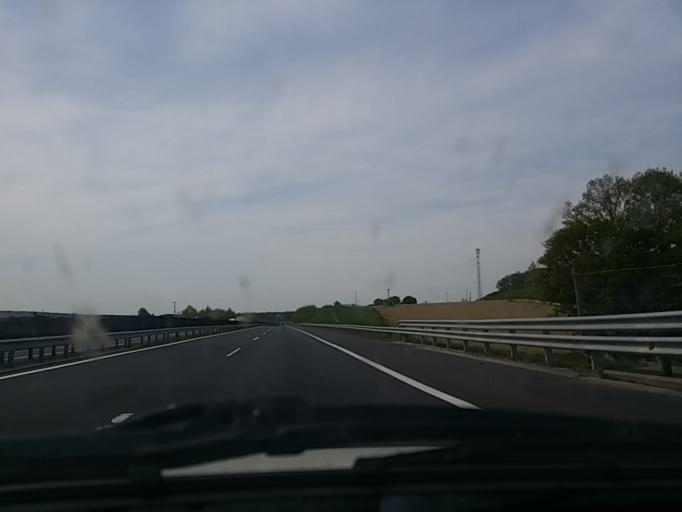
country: HU
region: Zala
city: Nagykanizsa
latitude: 46.4830
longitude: 17.0882
